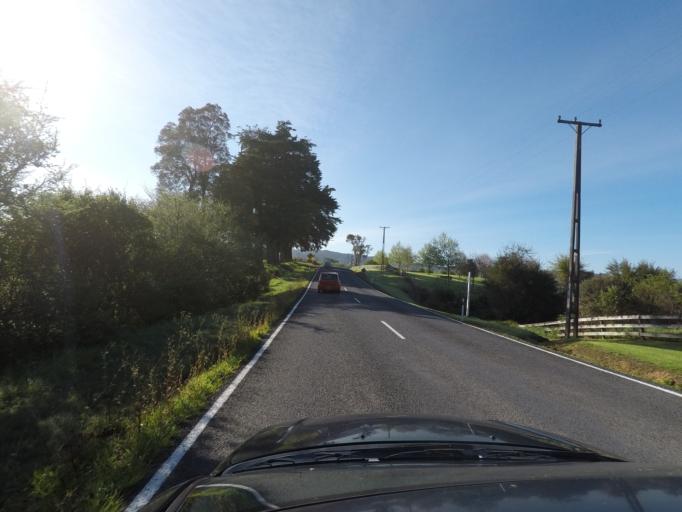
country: NZ
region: Auckland
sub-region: Auckland
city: Red Hill
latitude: -37.0019
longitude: 175.0412
